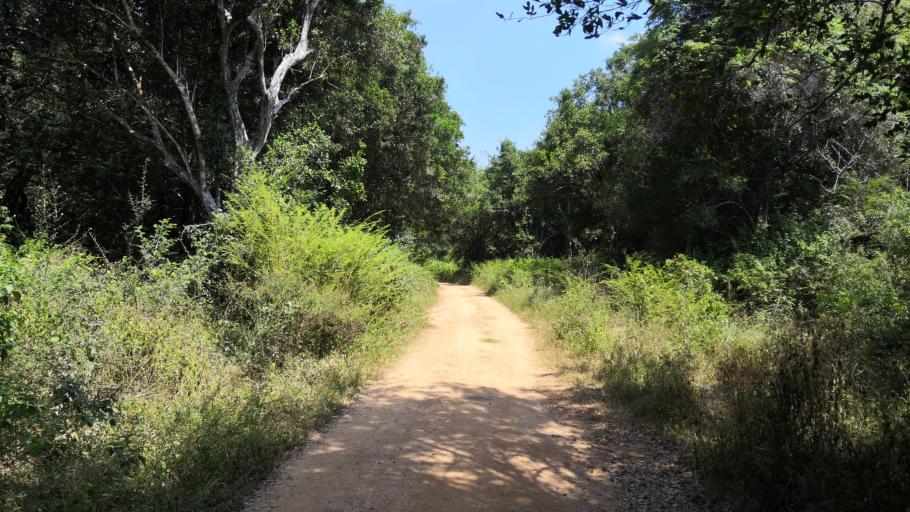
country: LK
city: Padaviya Divisional Secretariat
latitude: 8.9591
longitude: 80.6962
